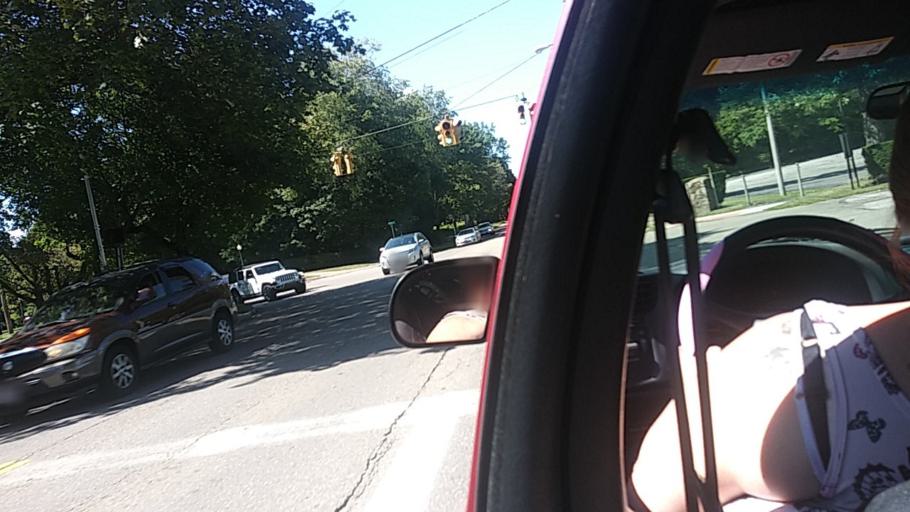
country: US
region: Ohio
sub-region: Summit County
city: Akron
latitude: 41.0995
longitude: -81.5560
